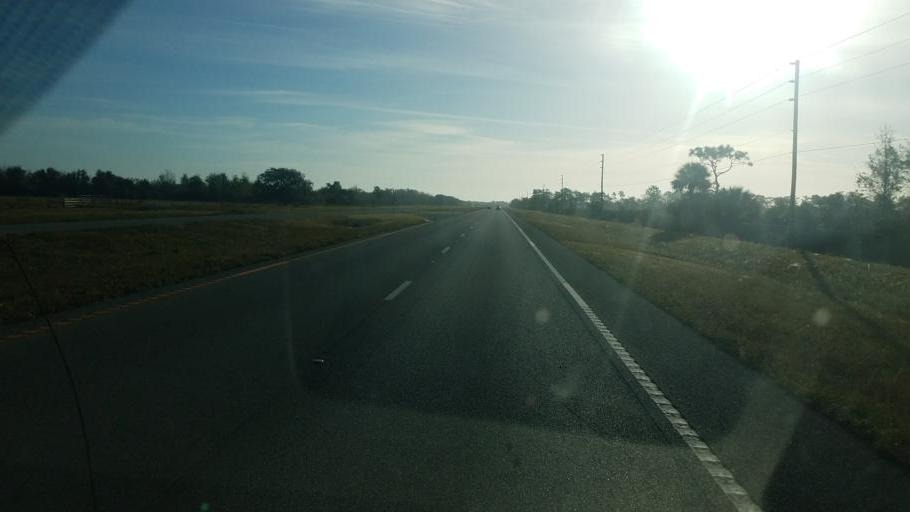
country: US
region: Florida
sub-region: Osceola County
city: Saint Cloud
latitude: 28.1297
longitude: -80.9969
